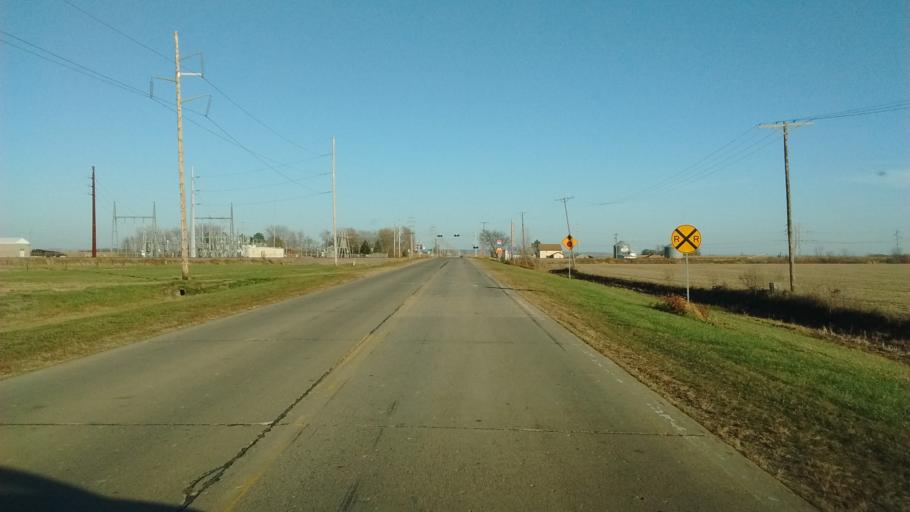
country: US
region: Iowa
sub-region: Woodbury County
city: Sergeant Bluff
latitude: 42.3302
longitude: -96.3047
